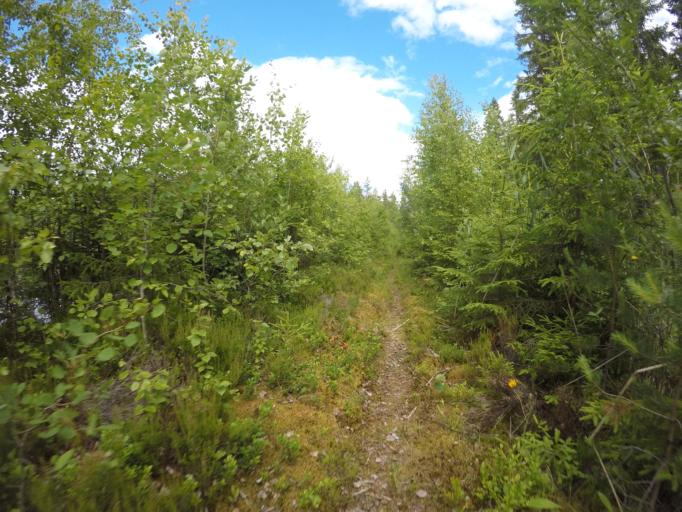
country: SE
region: OErebro
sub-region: Hallefors Kommun
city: Haellefors
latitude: 60.0445
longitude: 14.5067
